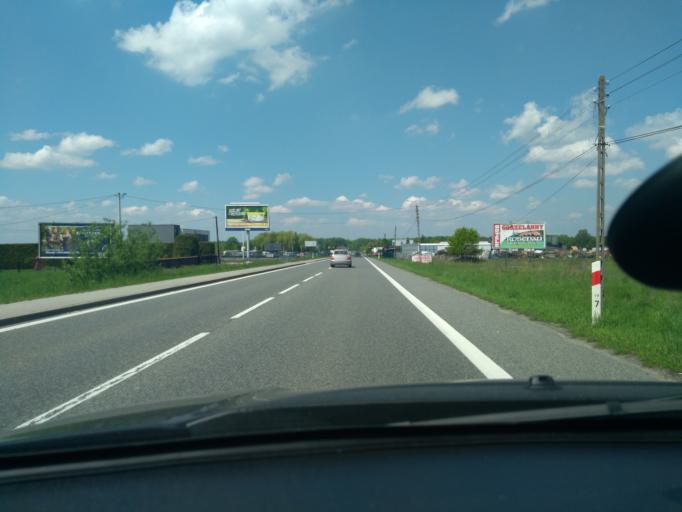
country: PL
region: Silesian Voivodeship
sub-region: Ruda Slaska
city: Ruda Slaska
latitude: 50.2051
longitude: 18.8566
